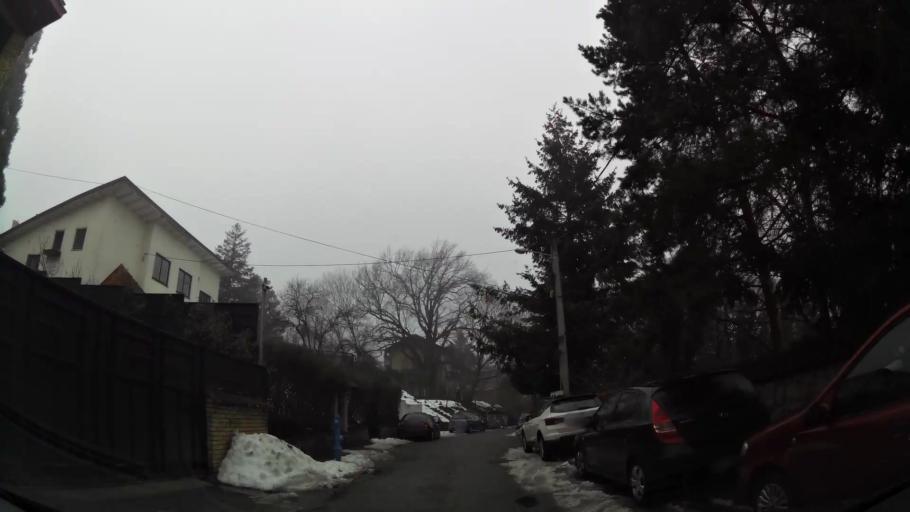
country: RS
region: Central Serbia
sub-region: Belgrade
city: Savski Venac
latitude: 44.7915
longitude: 20.4387
